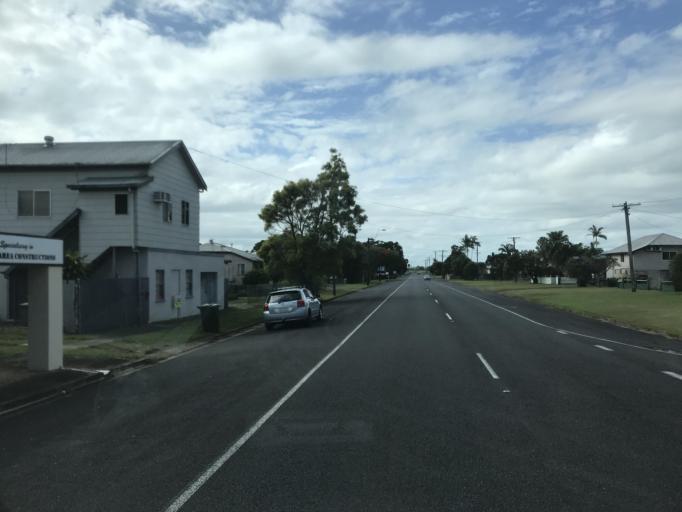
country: AU
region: Queensland
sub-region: Cassowary Coast
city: Innisfail
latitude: -17.5421
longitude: 146.0327
